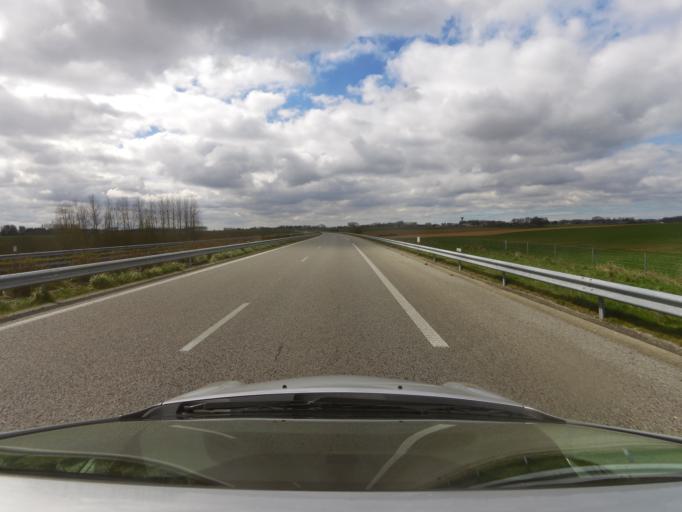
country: FR
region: Haute-Normandie
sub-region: Departement de la Seine-Maritime
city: Yebleron
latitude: 49.6135
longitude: 0.5229
